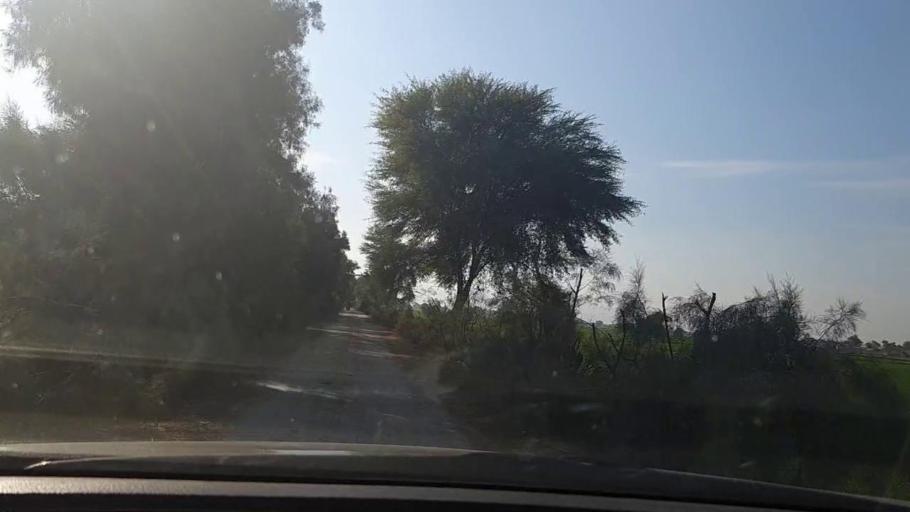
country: PK
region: Sindh
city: Sehwan
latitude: 26.3027
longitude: 67.9917
